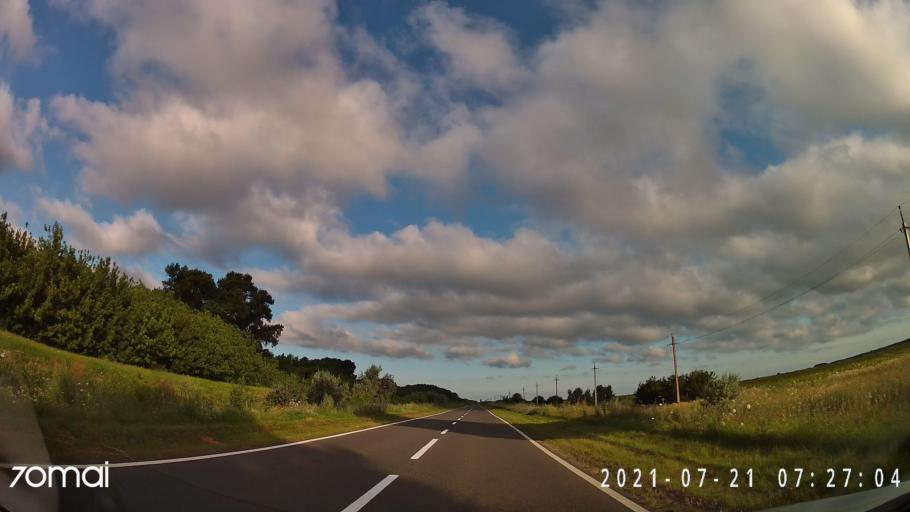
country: RO
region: Tulcea
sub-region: Oras Isaccea
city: Isaccea
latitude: 45.3012
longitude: 28.4255
